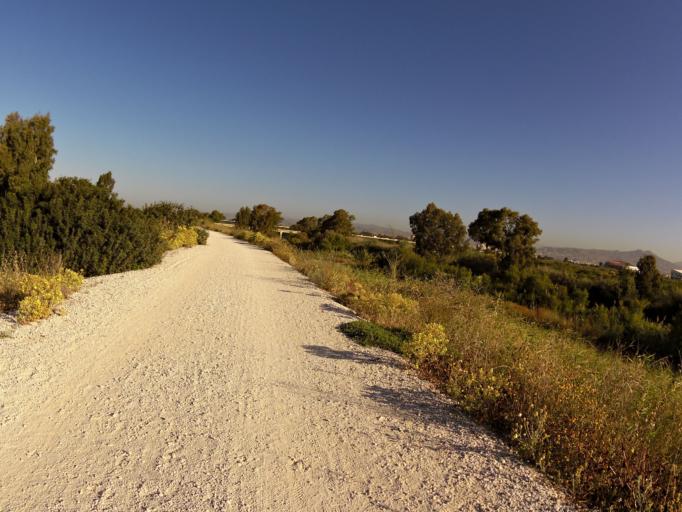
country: ES
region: Andalusia
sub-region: Provincia de Malaga
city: Malaga
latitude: 36.6705
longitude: -4.4604
